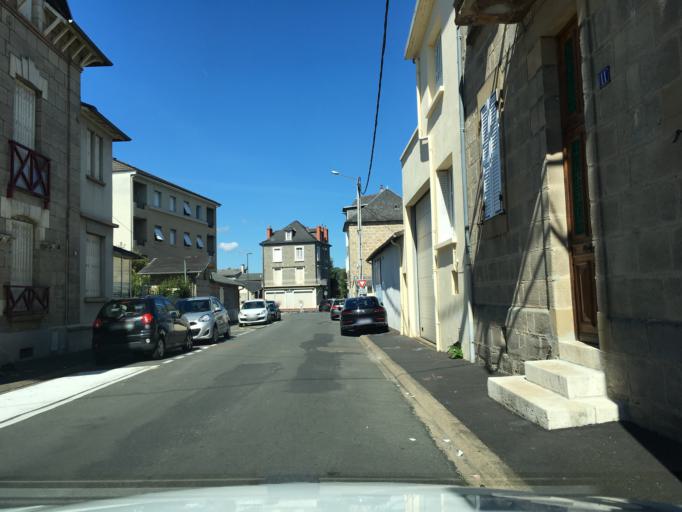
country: FR
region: Limousin
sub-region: Departement de la Correze
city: Brive-la-Gaillarde
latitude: 45.1568
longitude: 1.5415
